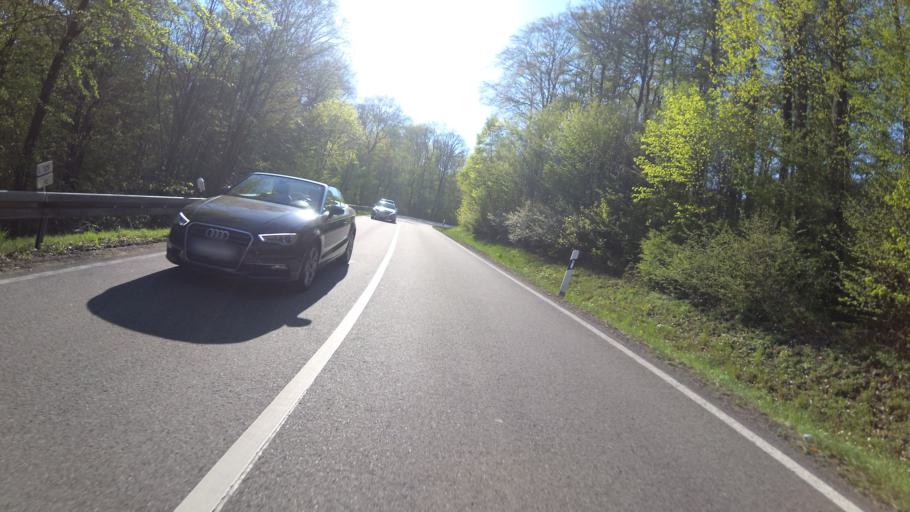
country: DE
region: Saarland
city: Friedrichsthal
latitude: 49.3562
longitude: 7.0873
